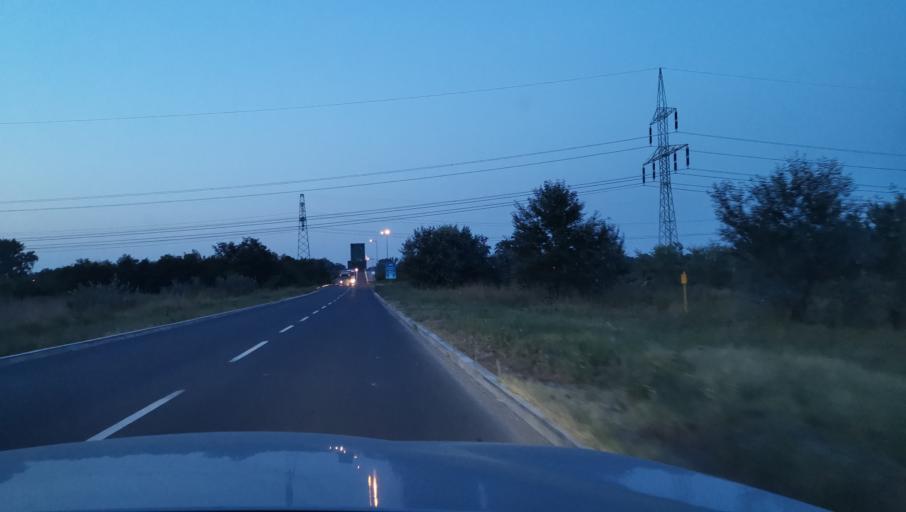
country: RS
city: Zvecka
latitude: 44.6688
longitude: 20.1638
